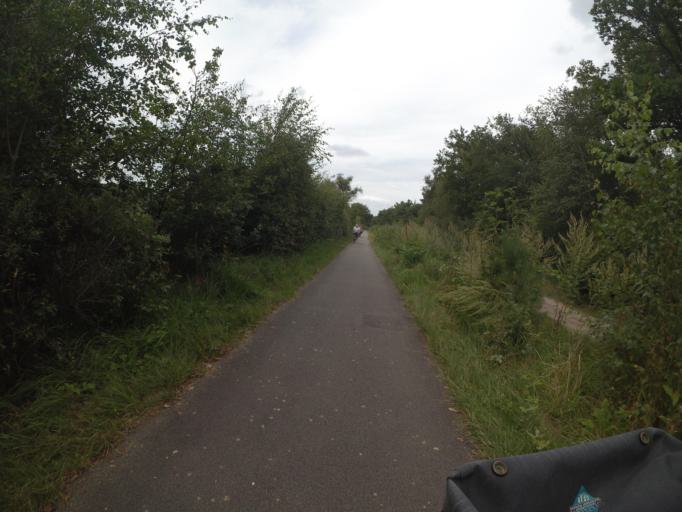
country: NL
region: North Brabant
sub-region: Gemeente Valkenswaard
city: Valkenswaard
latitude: 51.3259
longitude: 5.4507
